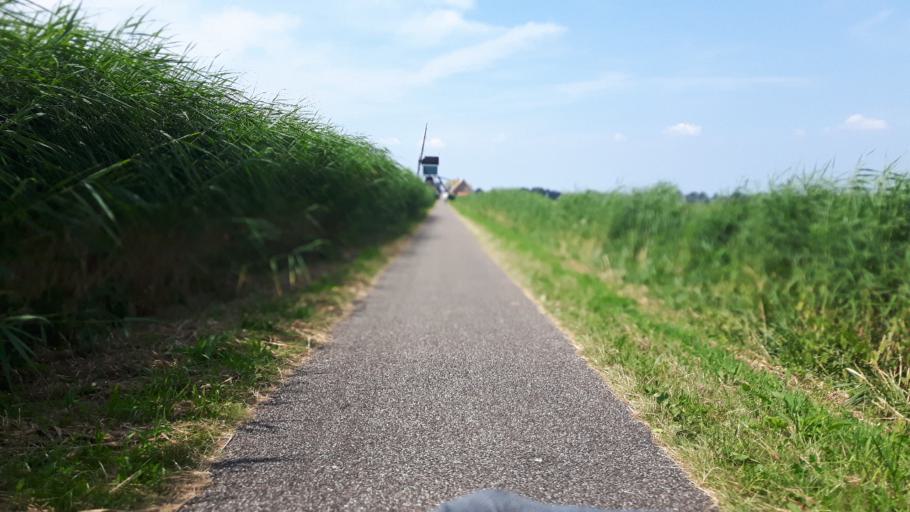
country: NL
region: South Holland
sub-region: Molenwaard
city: Liesveld
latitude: 51.9134
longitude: 4.8288
